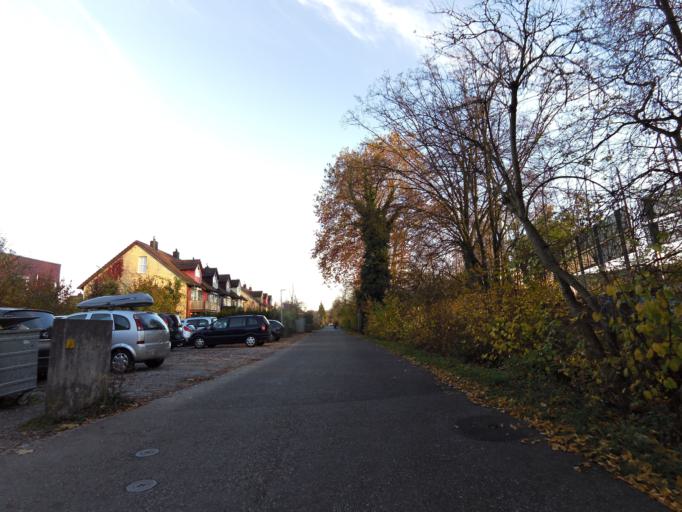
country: CH
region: Aargau
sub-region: Bezirk Aarau
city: Aarau
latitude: 47.3839
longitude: 8.0603
